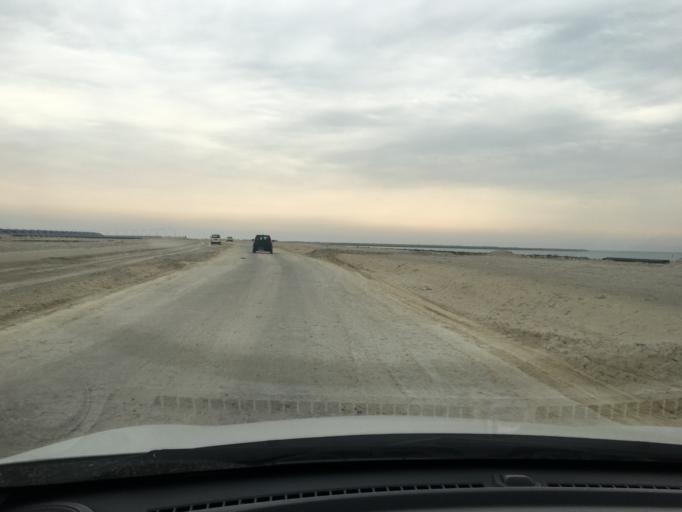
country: BH
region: Central Governorate
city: Dar Kulayb
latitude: 25.8316
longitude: 50.5944
